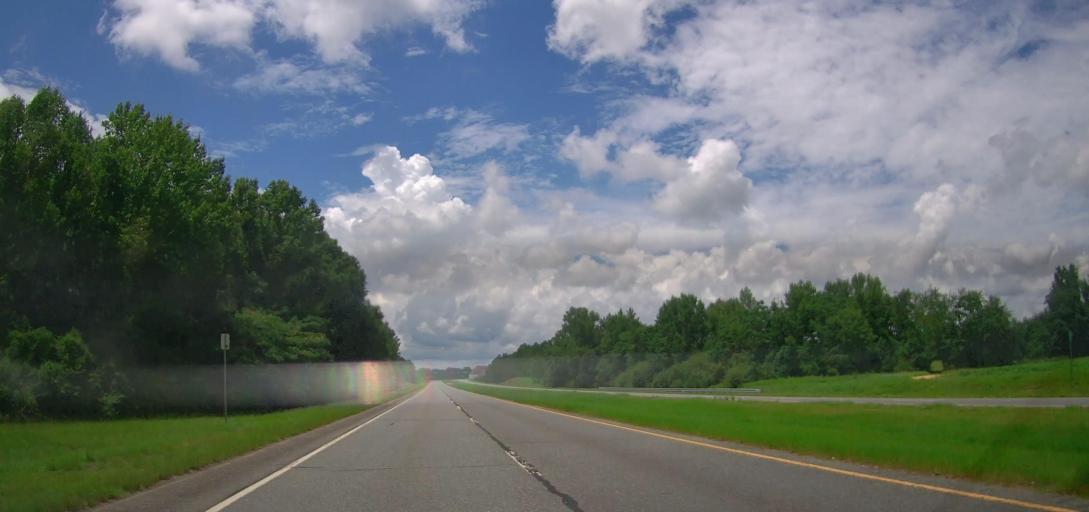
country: US
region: Georgia
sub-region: Dodge County
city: Eastman
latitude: 32.1908
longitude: -83.2051
